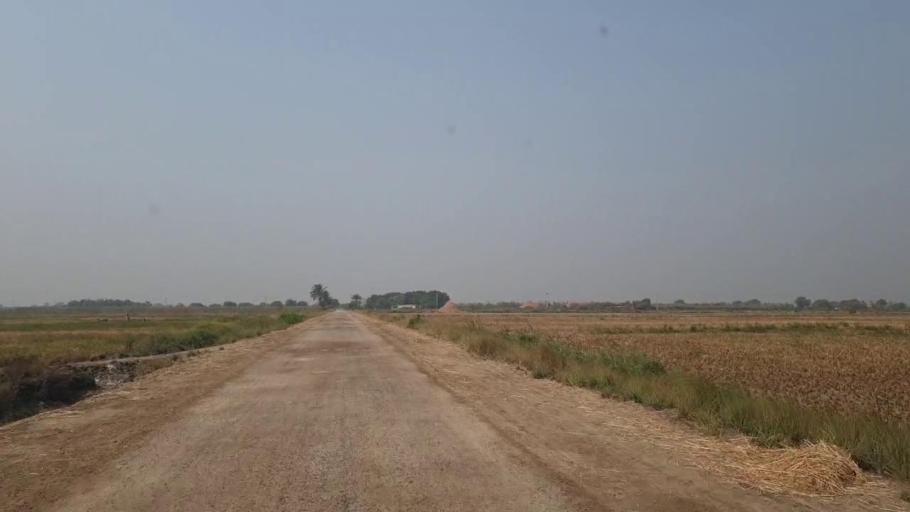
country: PK
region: Sindh
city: Matli
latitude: 25.1229
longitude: 68.6484
